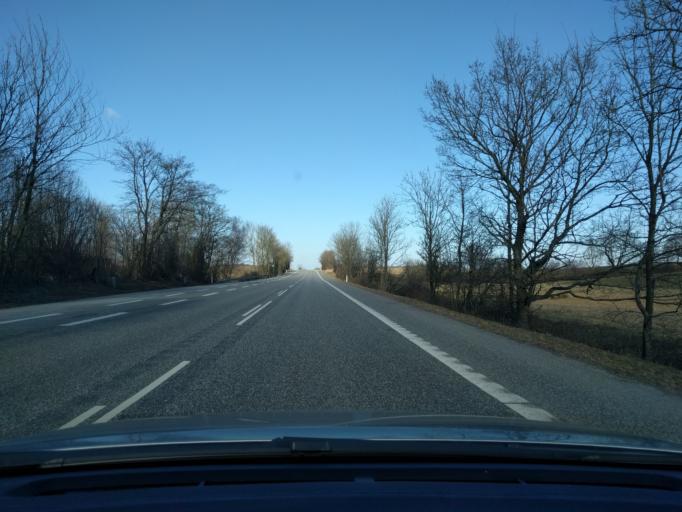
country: DK
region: South Denmark
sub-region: Aabenraa Kommune
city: Lojt Kirkeby
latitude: 55.1533
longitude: 9.4411
